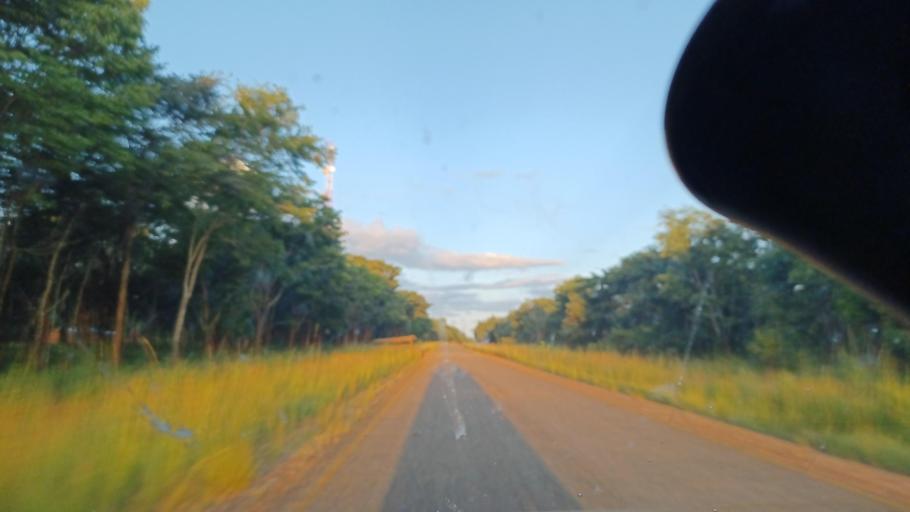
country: ZM
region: North-Western
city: Kasempa
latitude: -12.9871
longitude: 25.5621
